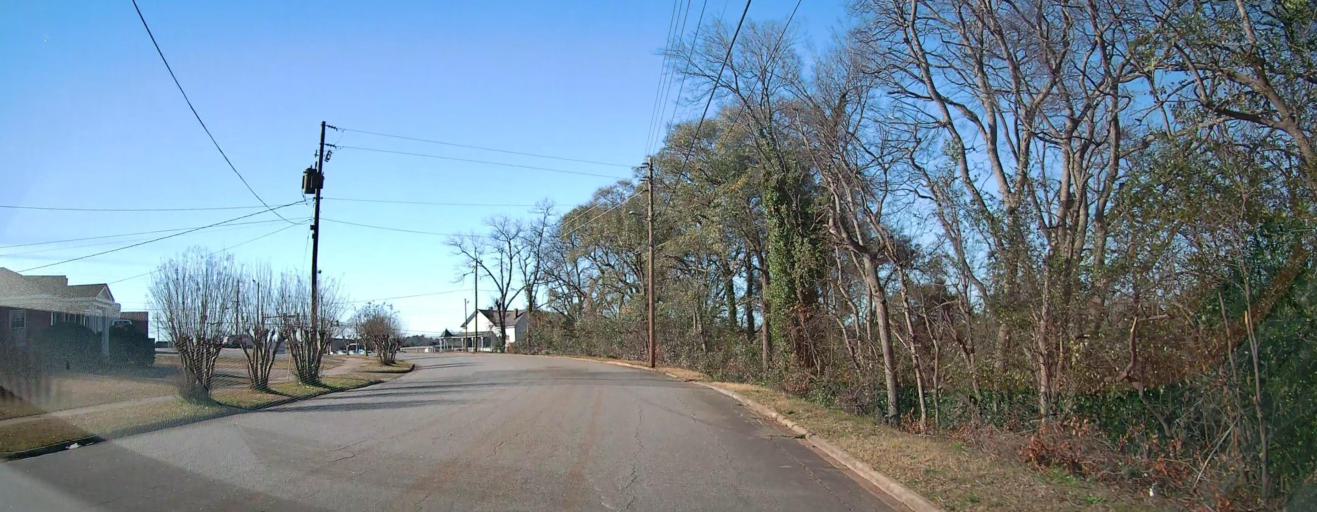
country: US
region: Georgia
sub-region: Sumter County
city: Americus
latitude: 32.0749
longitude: -84.2312
